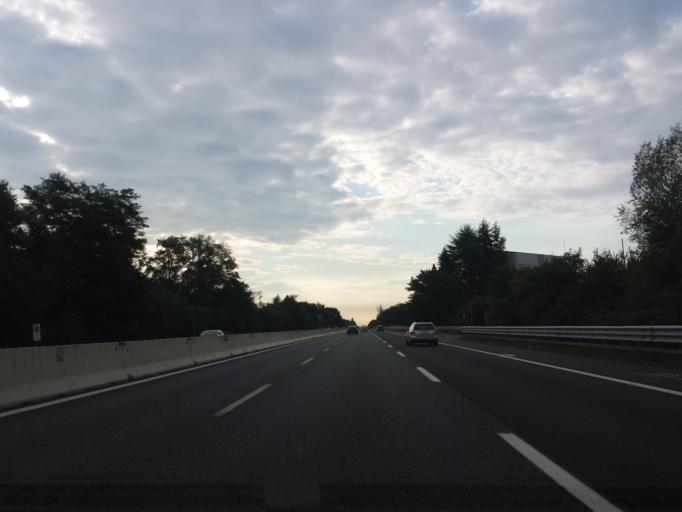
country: IT
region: Lombardy
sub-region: Provincia di Varese
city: Olgiate Olona
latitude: 45.6338
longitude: 8.8720
